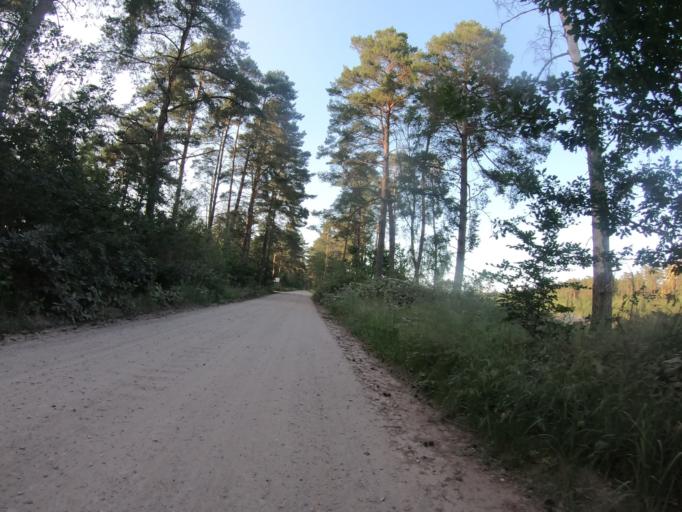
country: DE
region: Lower Saxony
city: Wagenhoff
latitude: 52.5381
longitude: 10.4952
